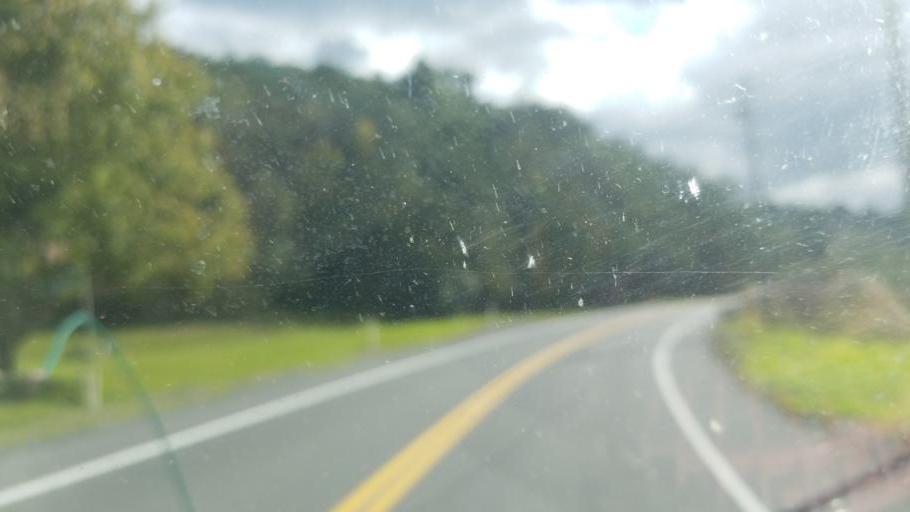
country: US
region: Pennsylvania
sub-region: Fulton County
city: McConnellsburg
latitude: 39.9873
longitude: -78.0588
